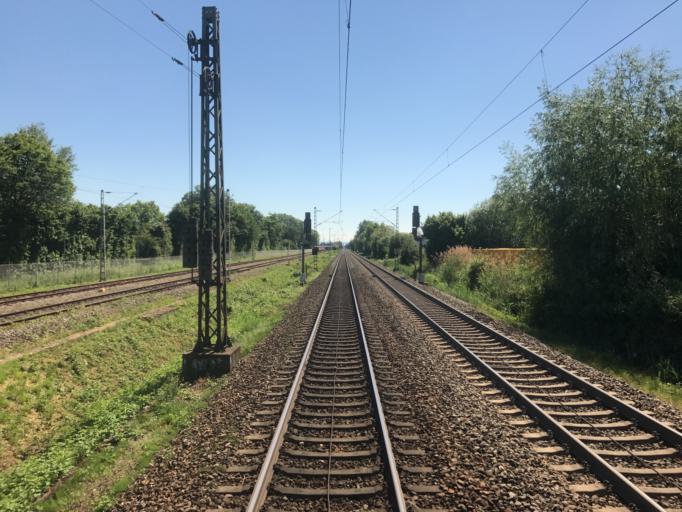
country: DE
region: Baden-Wuerttemberg
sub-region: Freiburg Region
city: Kippenheim
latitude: 48.3319
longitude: 7.8295
